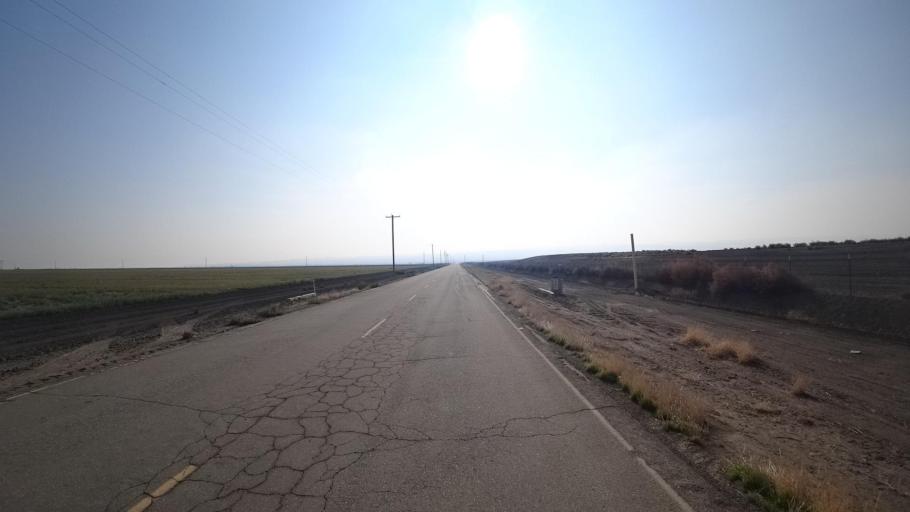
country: US
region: California
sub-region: Kern County
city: Buttonwillow
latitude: 35.3292
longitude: -119.3768
